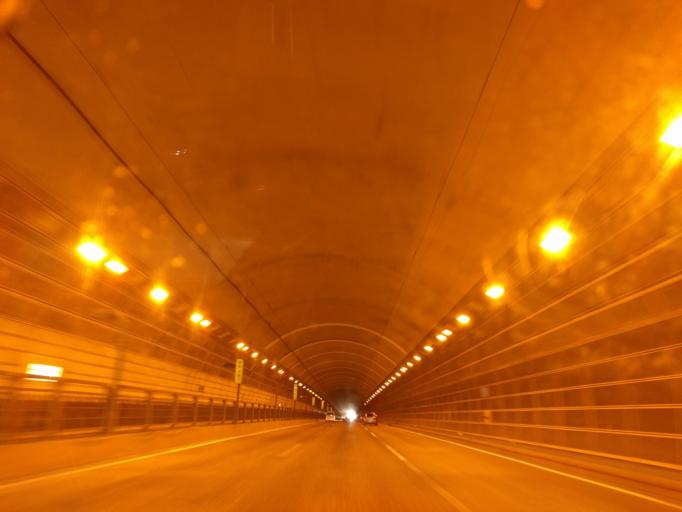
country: JP
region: Kanagawa
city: Yokohama
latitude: 35.3940
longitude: 139.5883
